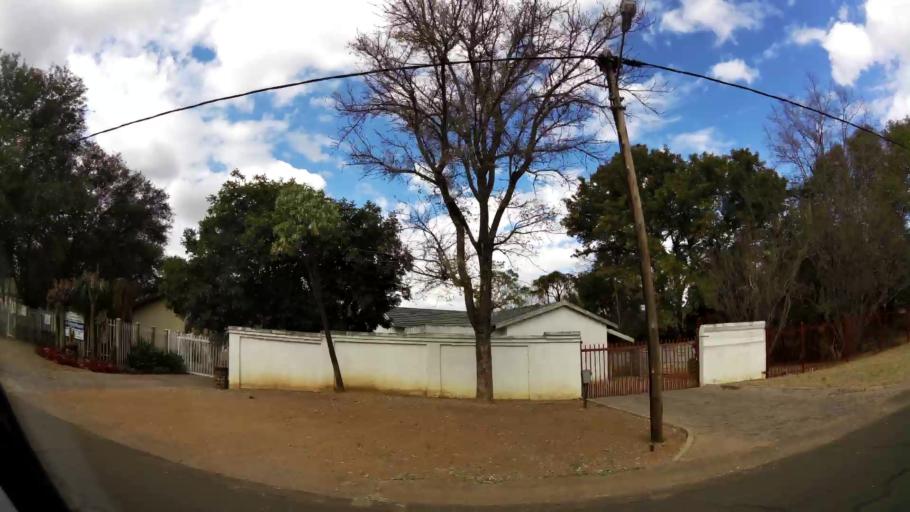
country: ZA
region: Limpopo
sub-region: Waterberg District Municipality
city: Modimolle
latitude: -24.7066
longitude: 28.4036
